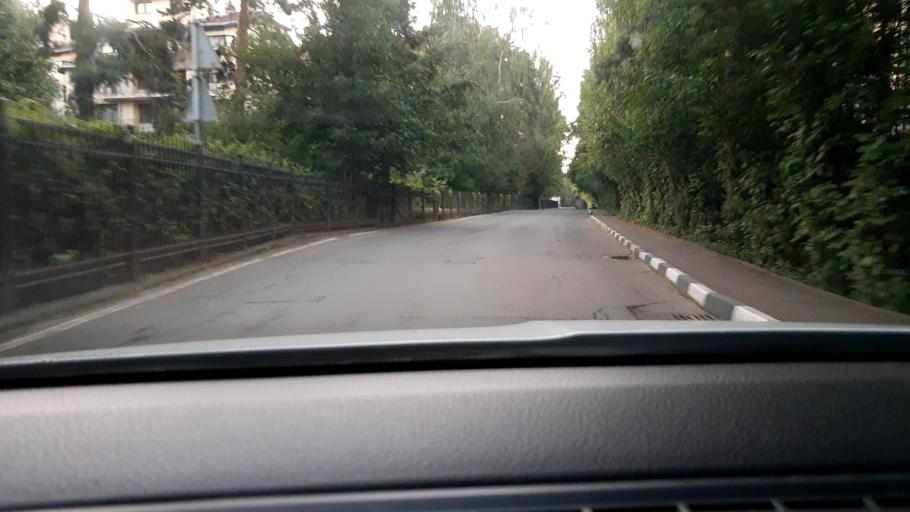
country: RU
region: Moskovskaya
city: Zarech'ye
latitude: 55.6822
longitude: 37.3848
